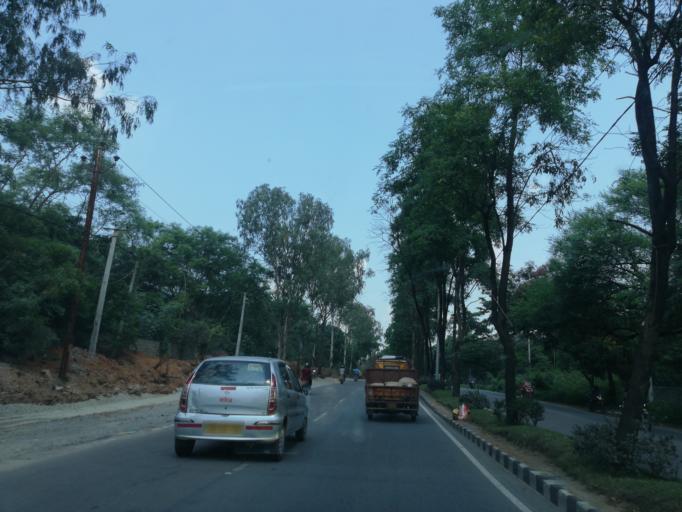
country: IN
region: Telangana
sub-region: Medak
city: Serilingampalle
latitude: 17.4531
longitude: 78.3433
